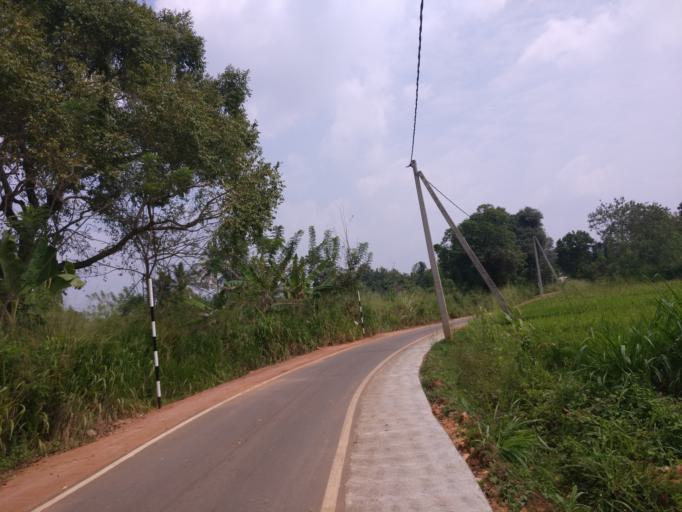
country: LK
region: Central
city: Dambulla
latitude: 7.8368
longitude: 80.6512
